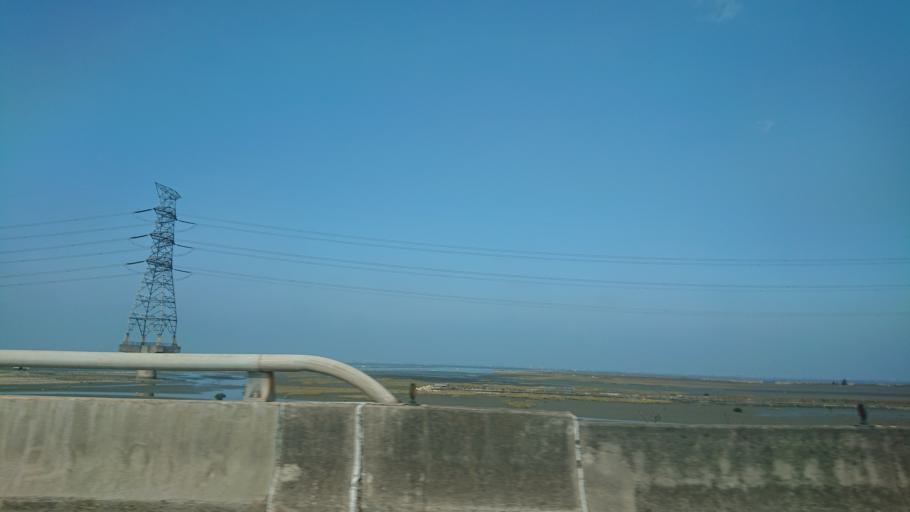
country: TW
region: Taiwan
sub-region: Changhua
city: Chang-hua
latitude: 24.1613
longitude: 120.4641
